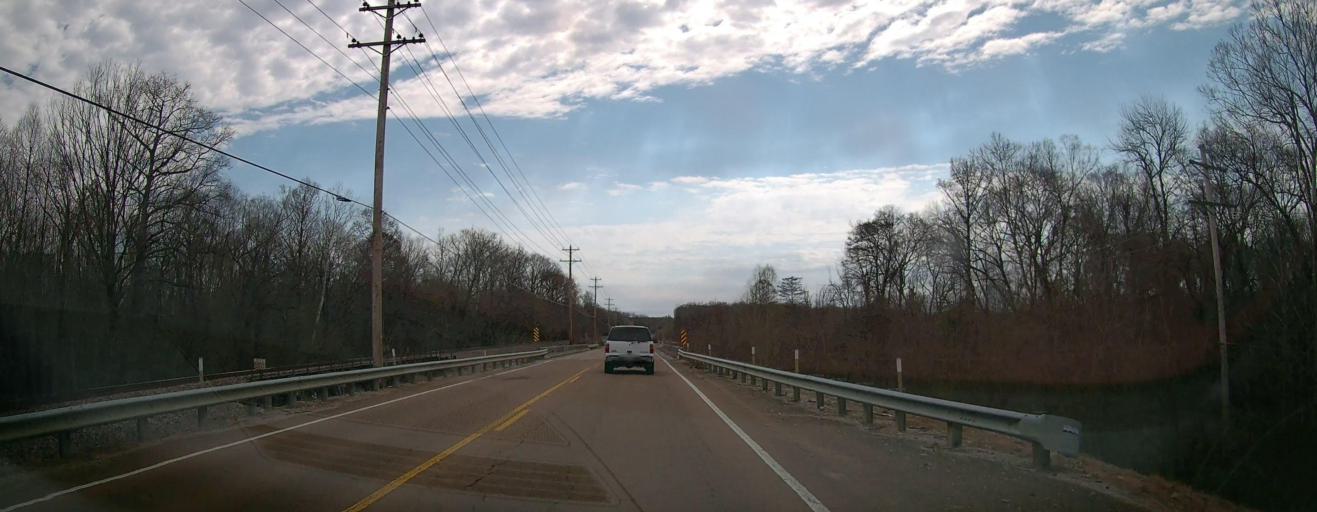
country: US
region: Mississippi
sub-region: Marshall County
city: Byhalia
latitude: 34.9068
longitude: -89.7523
